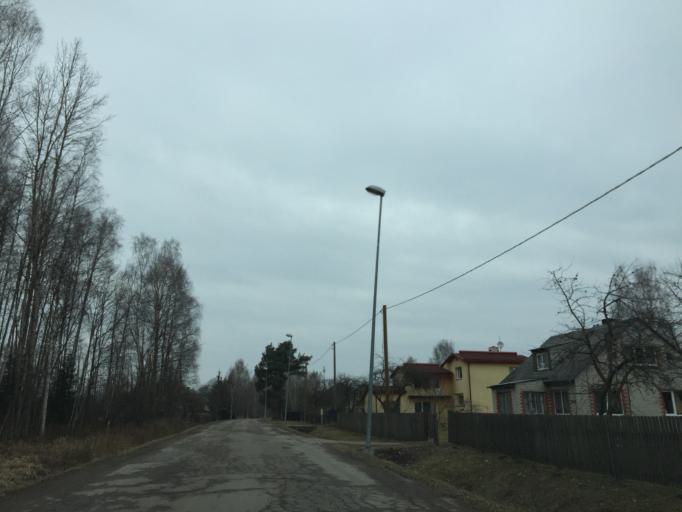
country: LV
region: Ozolnieku
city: Ozolnieki
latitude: 56.7172
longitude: 23.8337
